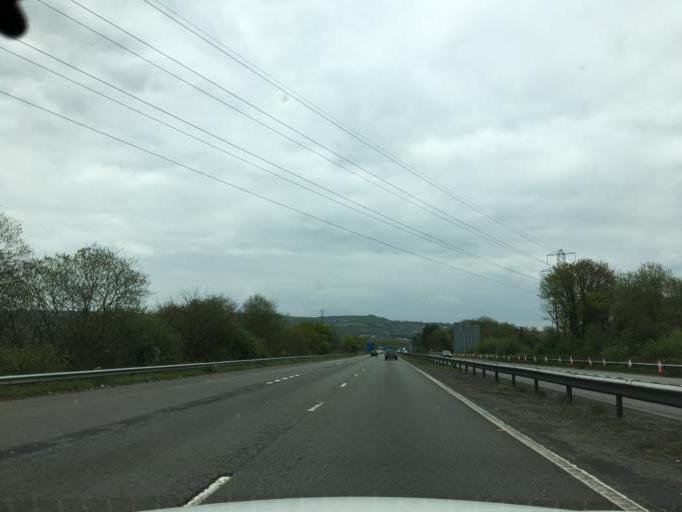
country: GB
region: Wales
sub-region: City and County of Swansea
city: Clydach
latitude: 51.6771
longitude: -3.9078
